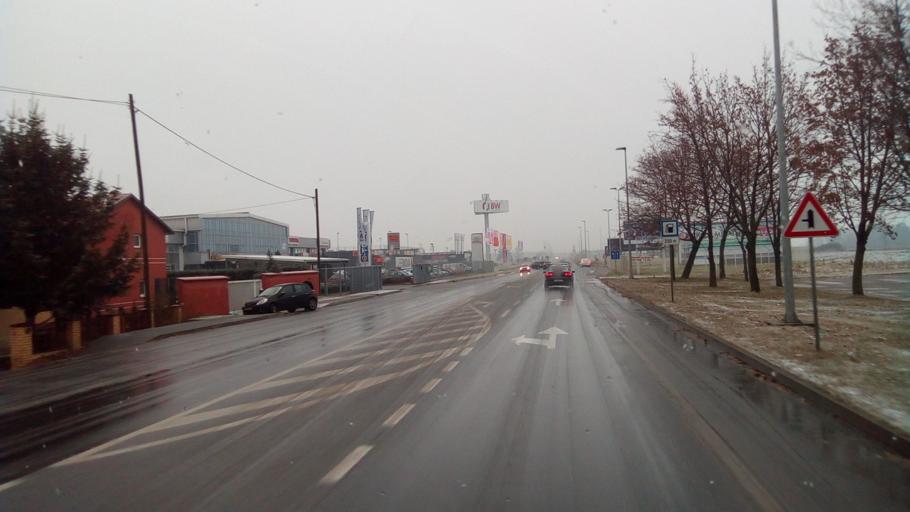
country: HR
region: Varazdinska
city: Varazdin
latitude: 46.3195
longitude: 16.3101
